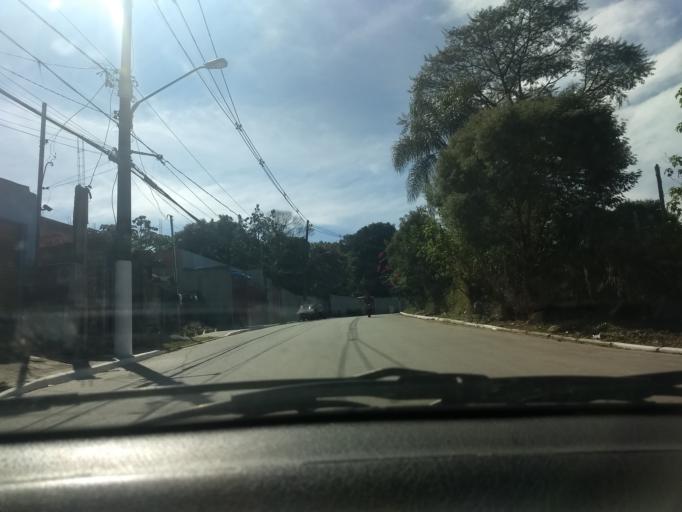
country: BR
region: Sao Paulo
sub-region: Embu-Guacu
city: Embu Guacu
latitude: -23.8243
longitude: -46.7077
